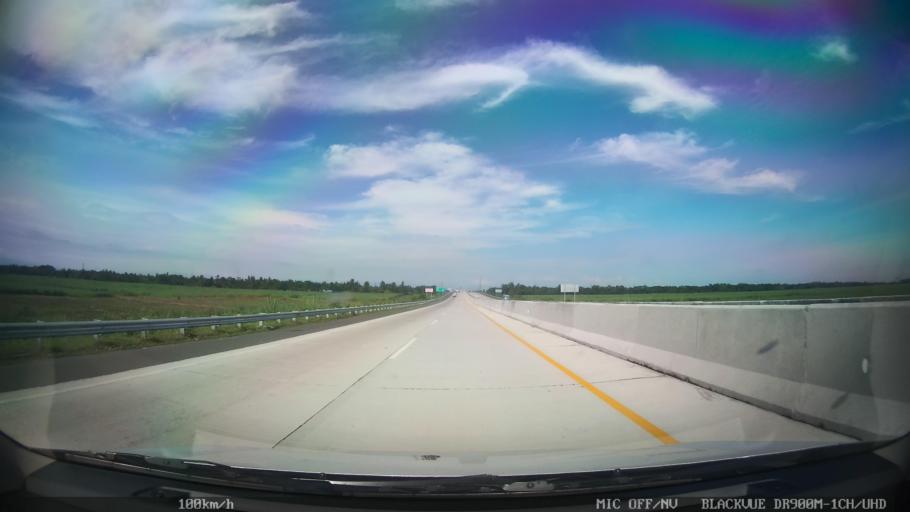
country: ID
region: North Sumatra
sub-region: Kabupaten Langkat
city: Stabat
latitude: 3.7134
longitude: 98.5151
